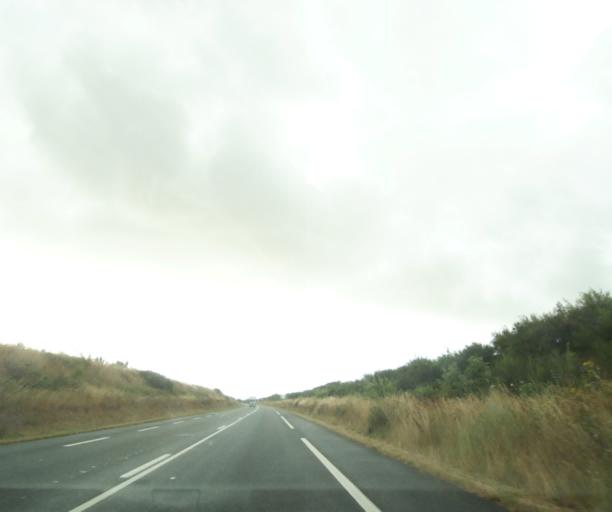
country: FR
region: Pays de la Loire
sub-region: Departement de la Vendee
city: Saint-Hilaire-de-Talmont
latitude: 46.4671
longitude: -1.6446
